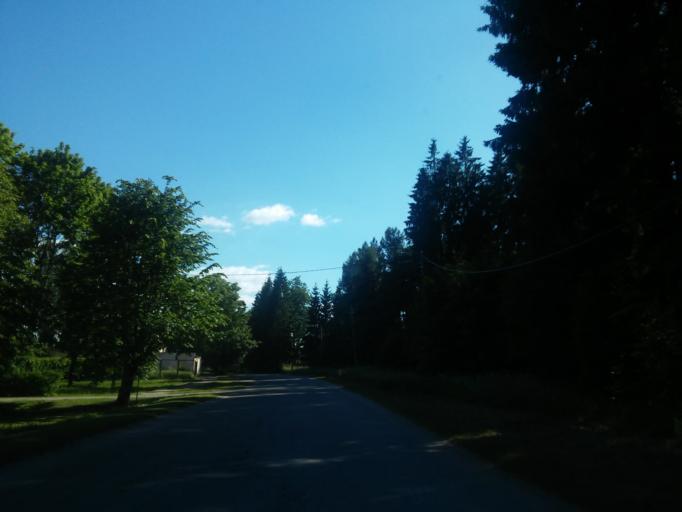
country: LV
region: Vainode
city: Vainode
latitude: 56.4355
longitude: 21.8734
